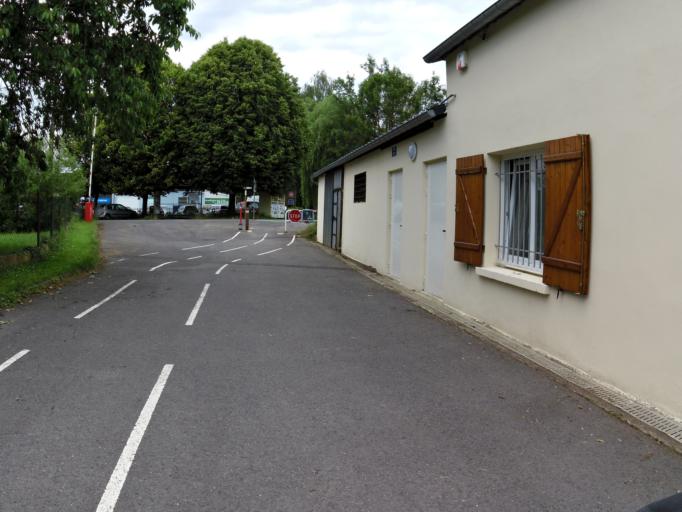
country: FR
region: Champagne-Ardenne
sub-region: Departement des Ardennes
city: Montcy-Notre-Dame
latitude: 49.7736
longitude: 4.7399
